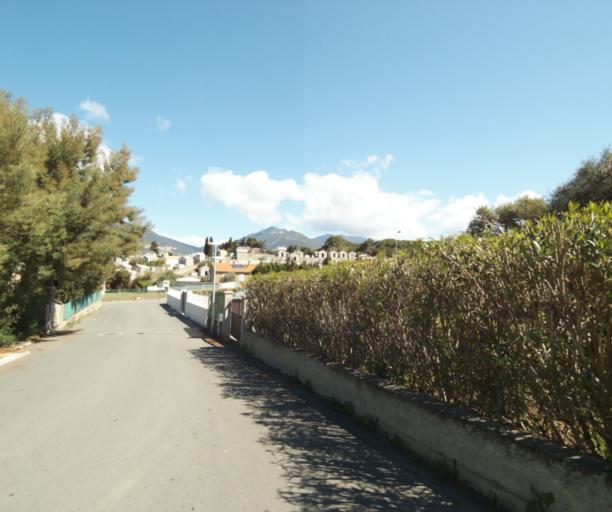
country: FR
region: Corsica
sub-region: Departement de la Corse-du-Sud
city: Propriano
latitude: 41.6773
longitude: 8.9128
